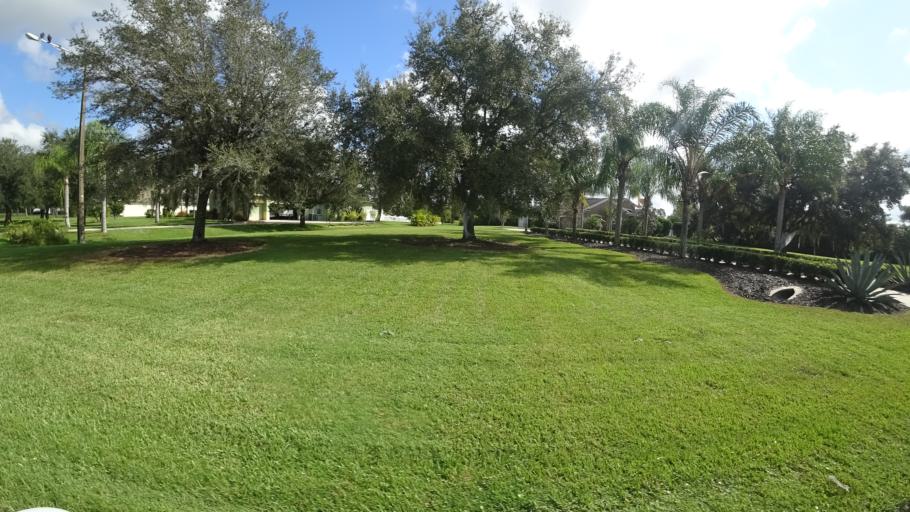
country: US
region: Florida
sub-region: Sarasota County
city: Fruitville
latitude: 27.3964
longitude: -82.3067
